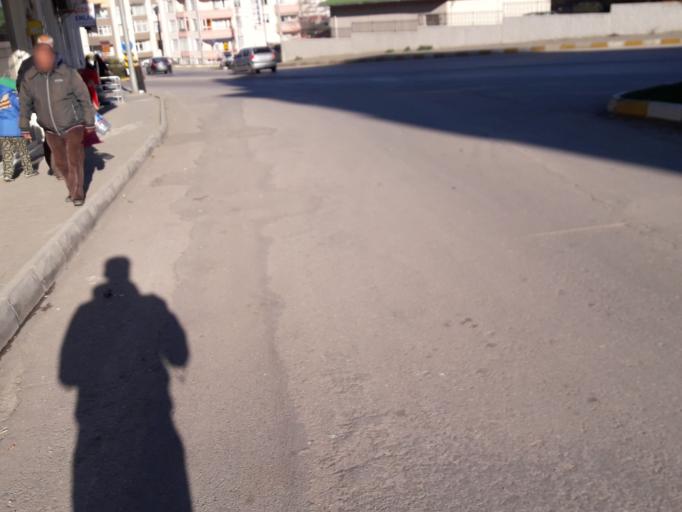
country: TR
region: Sinop
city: Sinop
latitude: 42.0219
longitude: 35.1351
